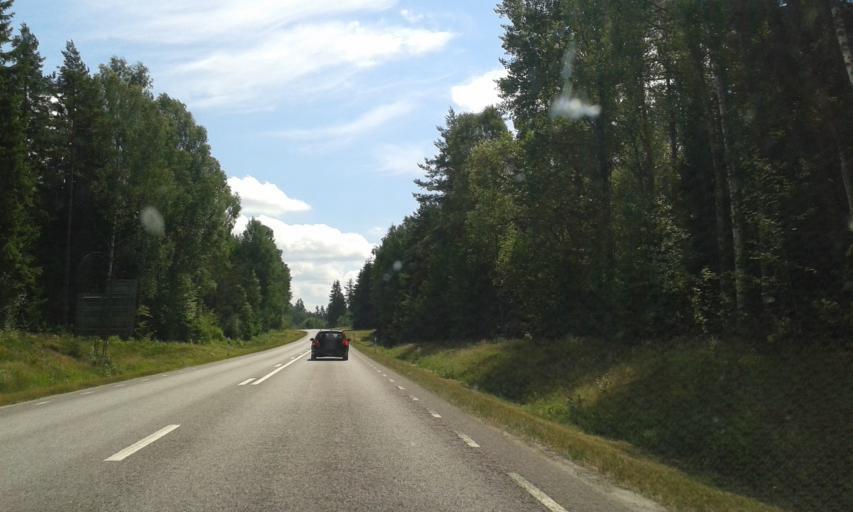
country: SE
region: Joenkoeping
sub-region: Varnamo Kommun
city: Rydaholm
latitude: 56.9802
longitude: 14.3056
